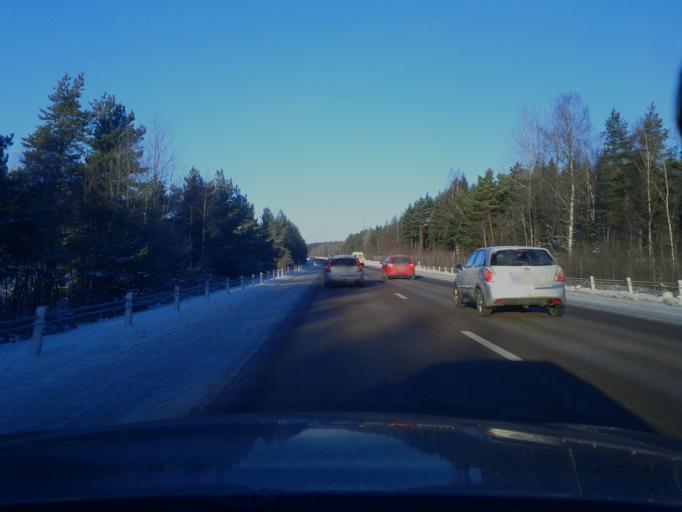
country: SE
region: Stockholm
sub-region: Sigtuna Kommun
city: Marsta
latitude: 59.6592
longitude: 17.8853
